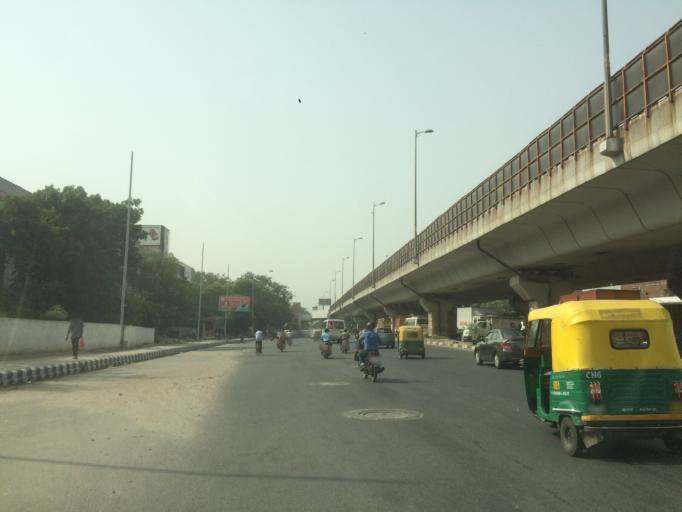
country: IN
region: NCT
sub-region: Central Delhi
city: Karol Bagh
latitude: 28.6281
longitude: 77.1338
